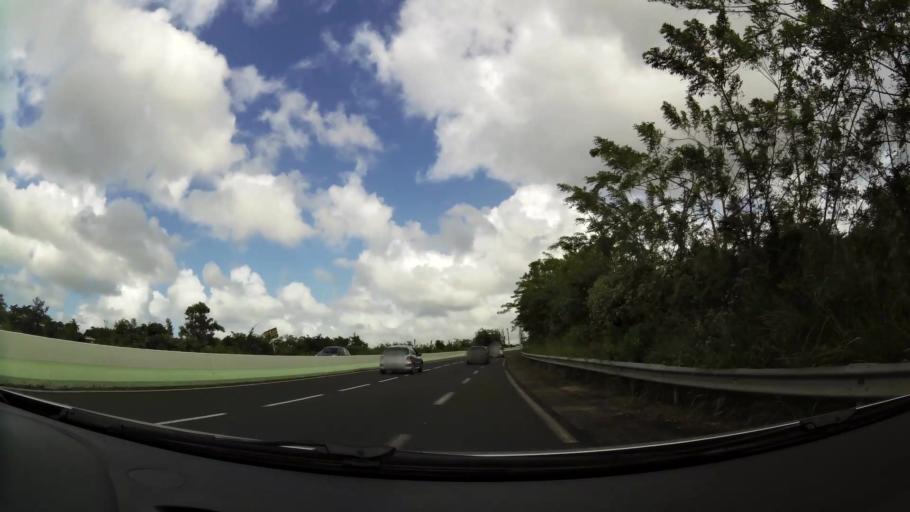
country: MQ
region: Martinique
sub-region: Martinique
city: Les Trois-Ilets
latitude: 14.5051
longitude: -60.9816
